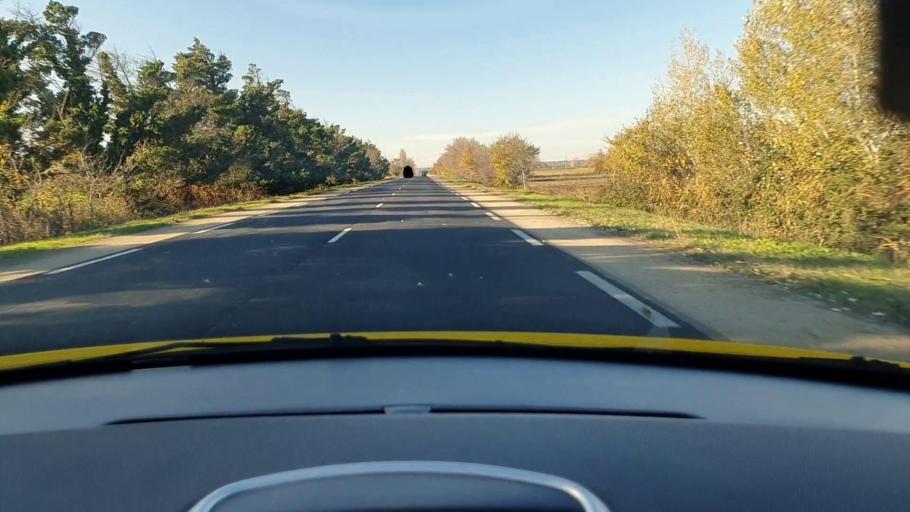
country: FR
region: Languedoc-Roussillon
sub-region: Departement du Gard
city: Fourques
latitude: 43.7035
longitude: 4.5680
